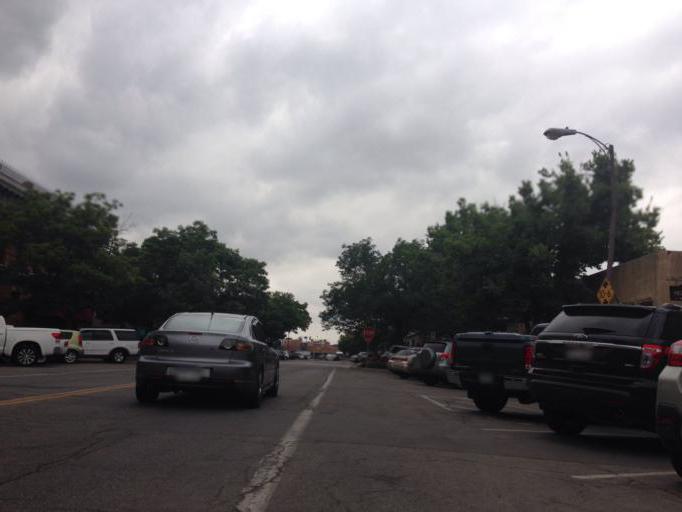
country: US
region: Colorado
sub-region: Larimer County
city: Fort Collins
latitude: 40.5876
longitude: -105.0748
